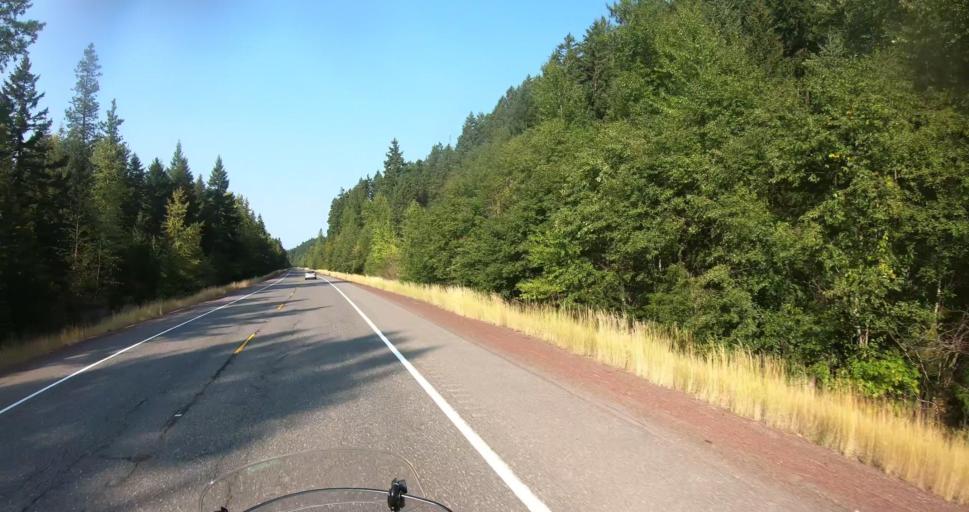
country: US
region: Oregon
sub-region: Hood River County
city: Odell
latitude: 45.4755
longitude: -121.5611
